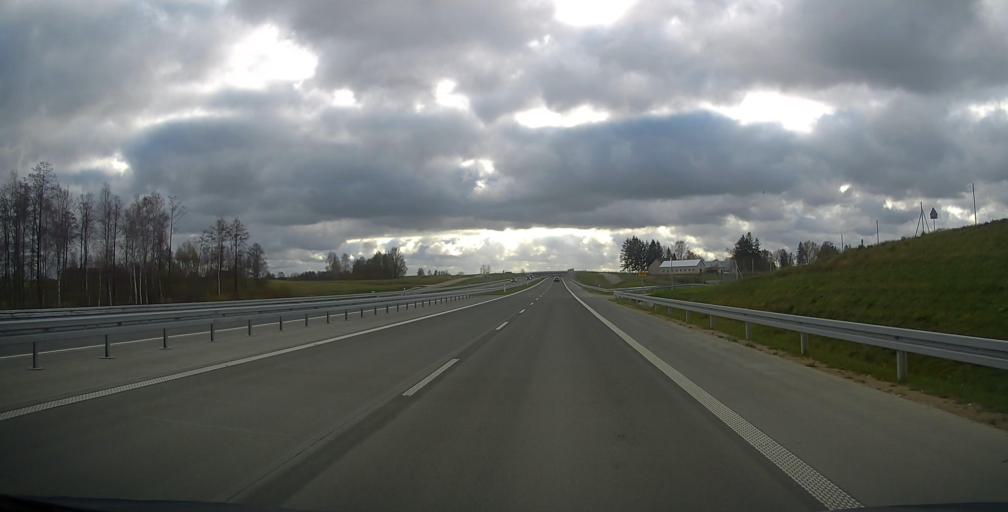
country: PL
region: Podlasie
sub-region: Powiat suwalski
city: Raczki
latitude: 53.9481
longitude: 22.7656
